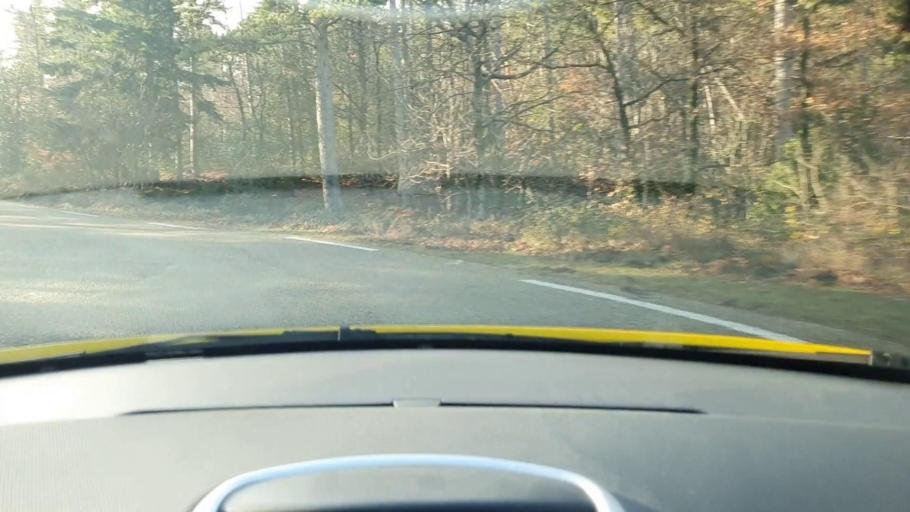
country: FR
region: Languedoc-Roussillon
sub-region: Departement du Gard
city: Branoux-les-Taillades
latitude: 44.3517
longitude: 3.9324
